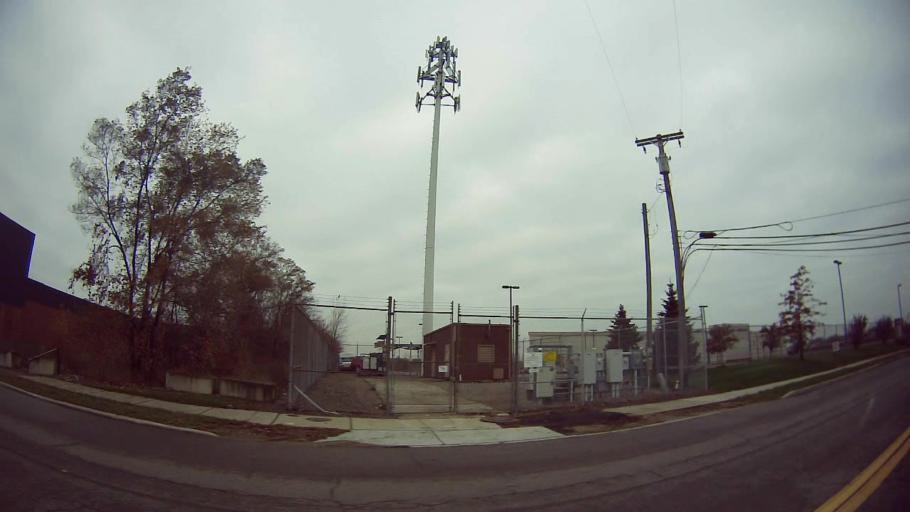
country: US
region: Michigan
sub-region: Wayne County
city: Highland Park
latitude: 42.4162
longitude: -83.0819
